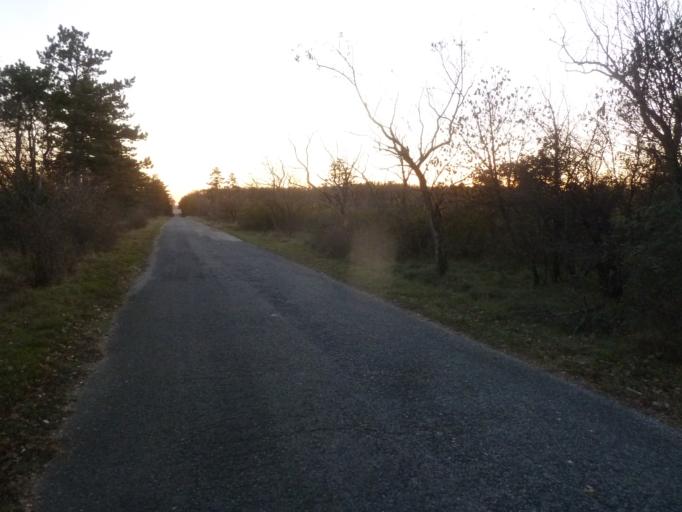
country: HU
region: Fejer
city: Zamoly
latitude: 47.3521
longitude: 18.3417
